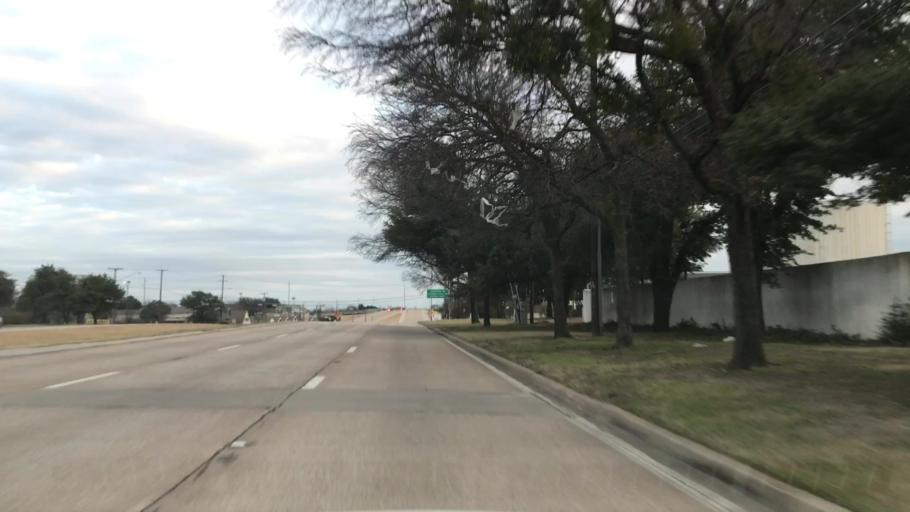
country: US
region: Texas
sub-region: Dallas County
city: Cockrell Hill
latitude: 32.6968
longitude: -96.8962
